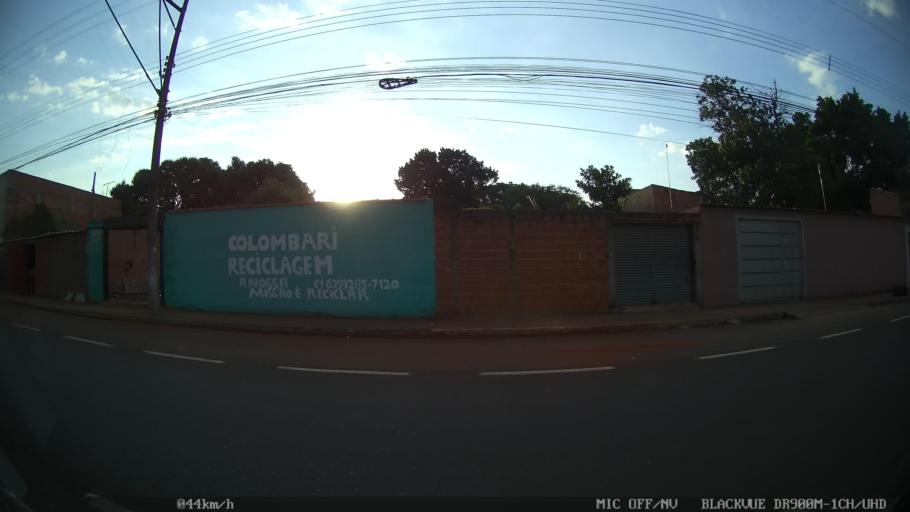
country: BR
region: Sao Paulo
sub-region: Ribeirao Preto
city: Ribeirao Preto
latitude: -21.1482
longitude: -47.8079
